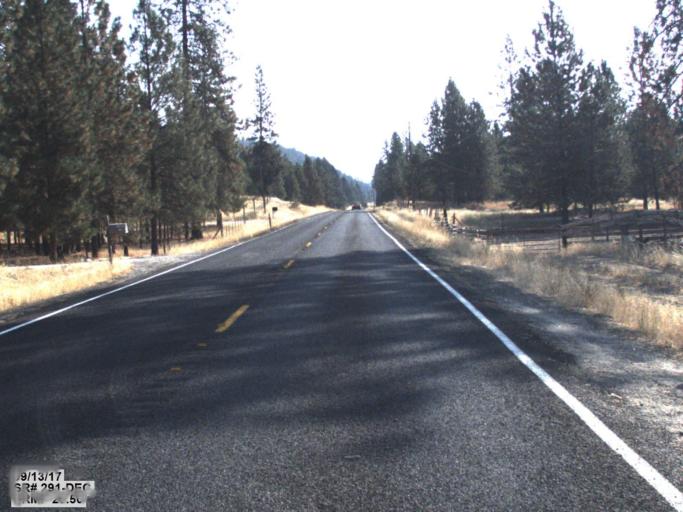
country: US
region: Washington
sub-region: Spokane County
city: Fairchild Air Force Base
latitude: 47.8392
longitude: -117.7847
